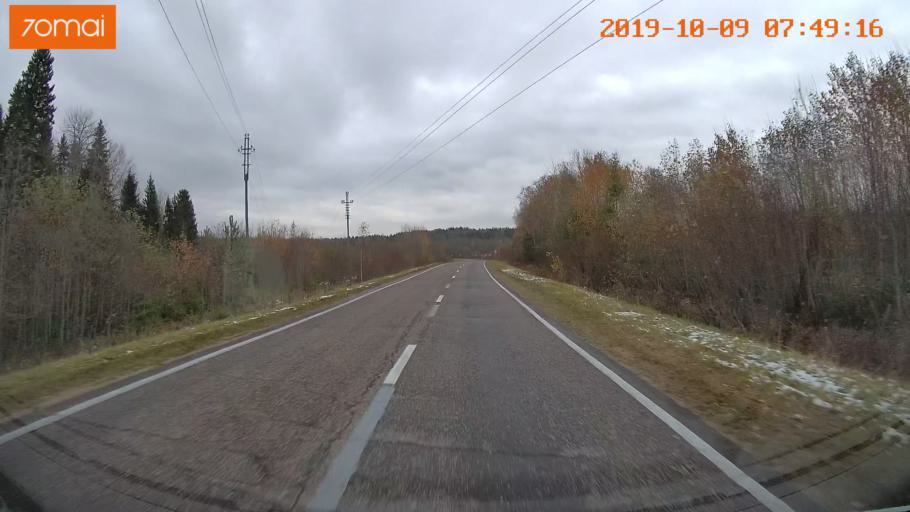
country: RU
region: Jaroslavl
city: Kukoboy
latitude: 58.6676
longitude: 39.8434
